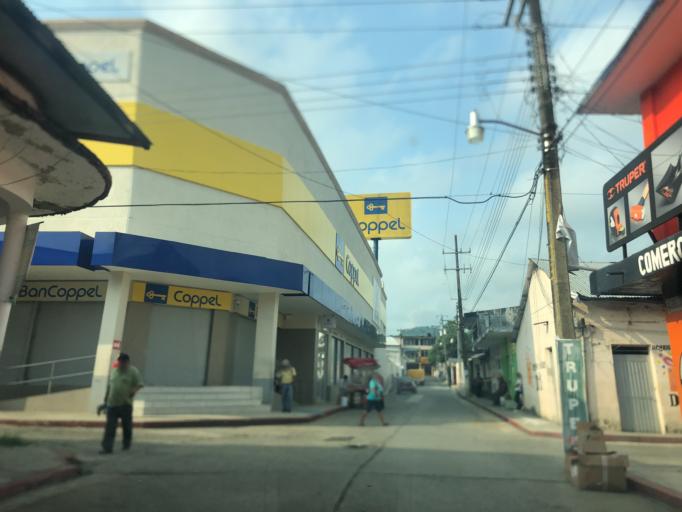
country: MX
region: Chiapas
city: Pichucalco
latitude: 17.5100
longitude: -93.1166
